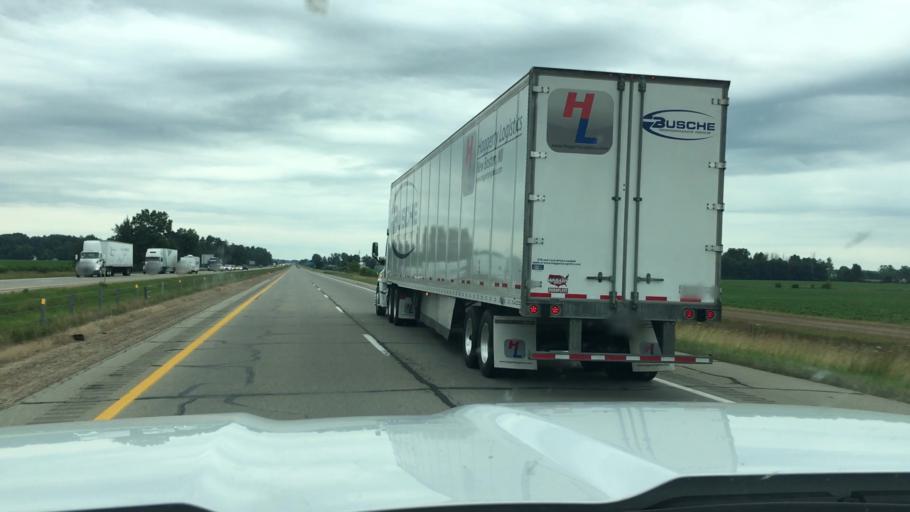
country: US
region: Michigan
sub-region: Allegan County
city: Wayland
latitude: 42.6571
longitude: -85.6621
